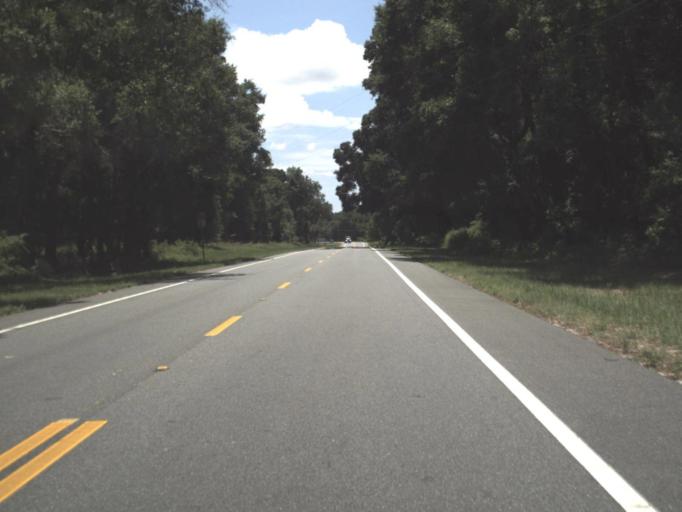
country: US
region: Florida
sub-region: Dixie County
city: Cross City
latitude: 29.8437
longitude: -82.9668
